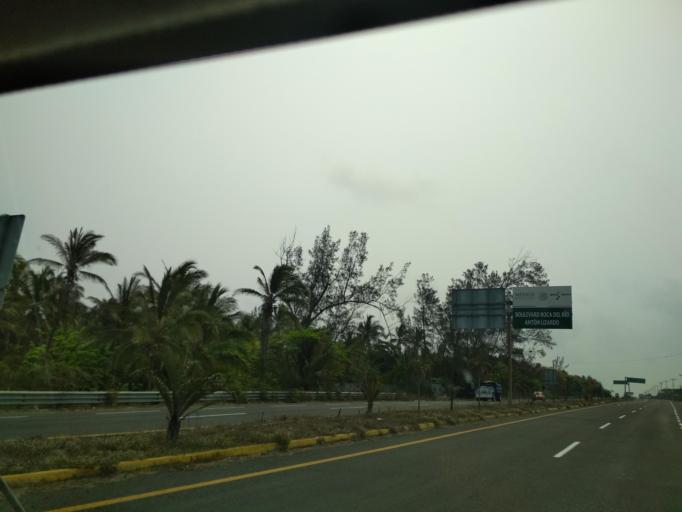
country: MX
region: Veracruz
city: Anton Lizardo
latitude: 19.0521
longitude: -96.0184
